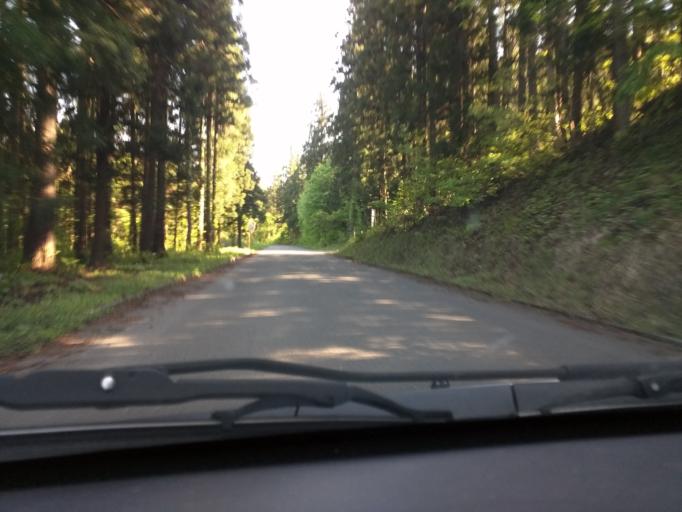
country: JP
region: Fukushima
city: Kitakata
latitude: 37.4839
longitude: 139.6691
